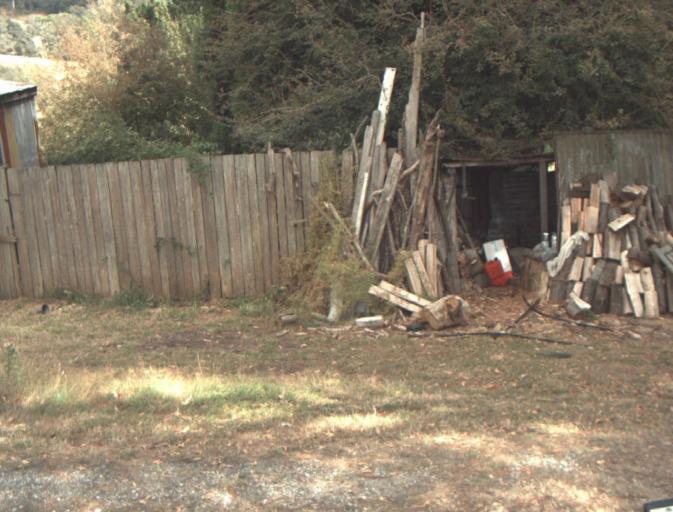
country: AU
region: Tasmania
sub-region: Launceston
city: Mayfield
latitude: -41.2188
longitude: 147.1065
